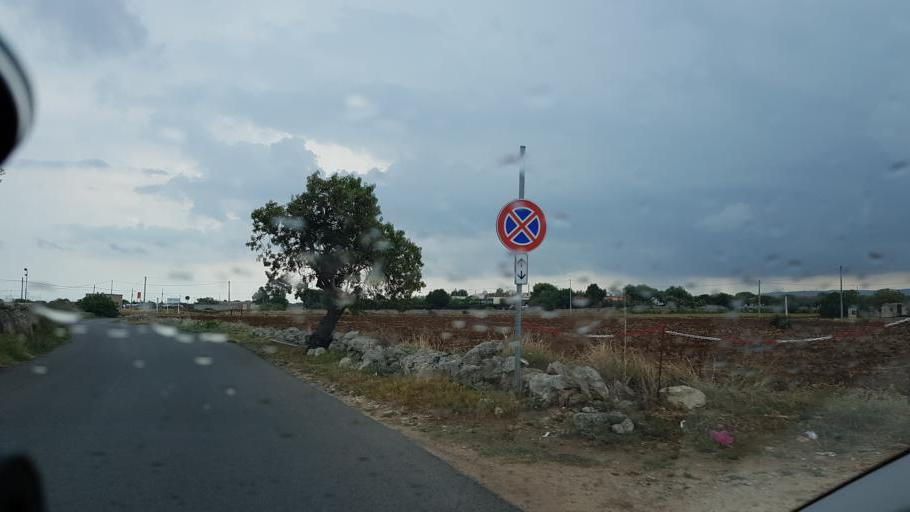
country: IT
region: Apulia
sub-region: Provincia di Bari
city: Monopoli
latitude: 40.9349
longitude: 17.3206
